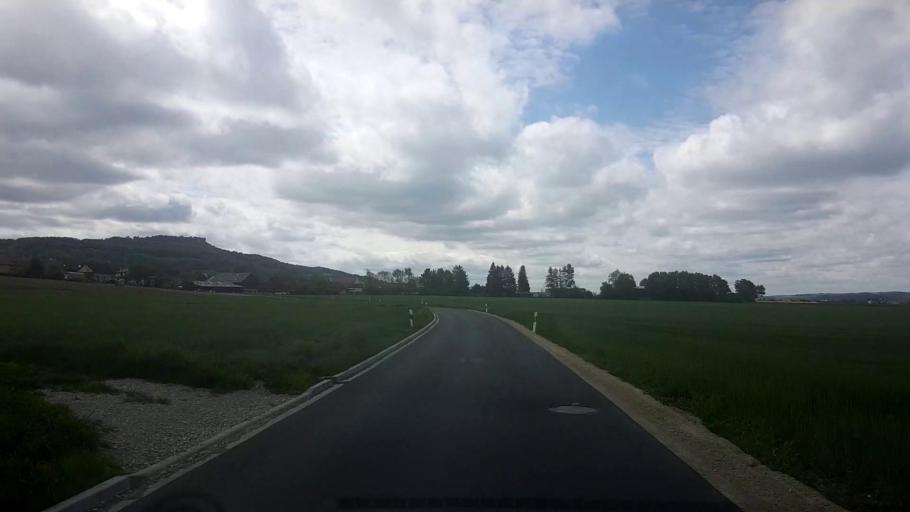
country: DE
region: Bavaria
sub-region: Upper Franconia
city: Bad Staffelstein
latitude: 50.1196
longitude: 11.0319
